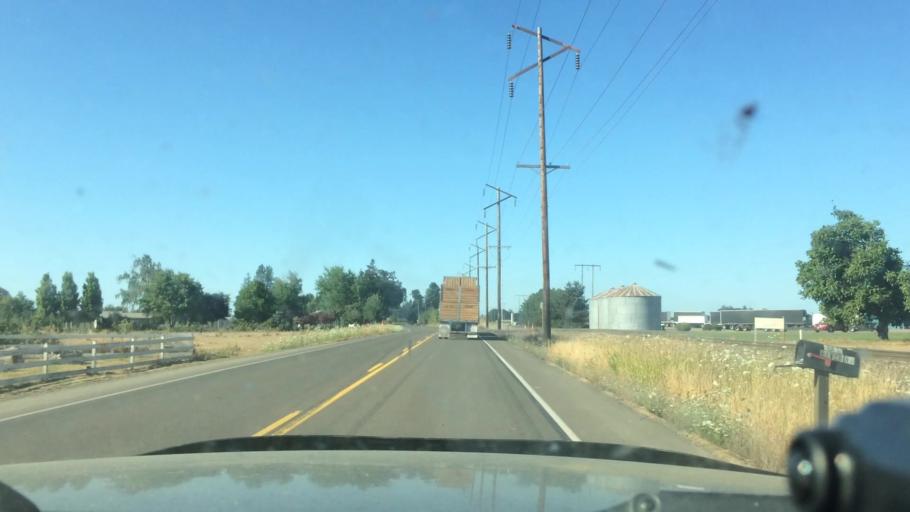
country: US
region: Oregon
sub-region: Marion County
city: Hayesville
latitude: 45.0589
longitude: -122.9828
